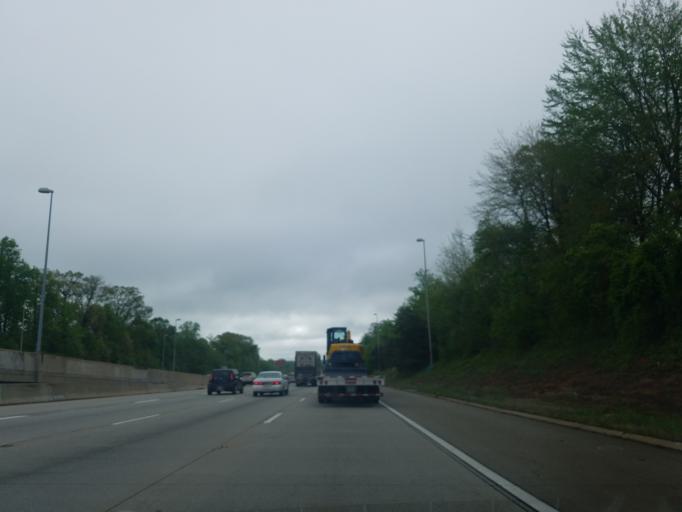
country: US
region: Virginia
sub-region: Fairfax County
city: Greenbriar
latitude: 38.8592
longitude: -77.3618
